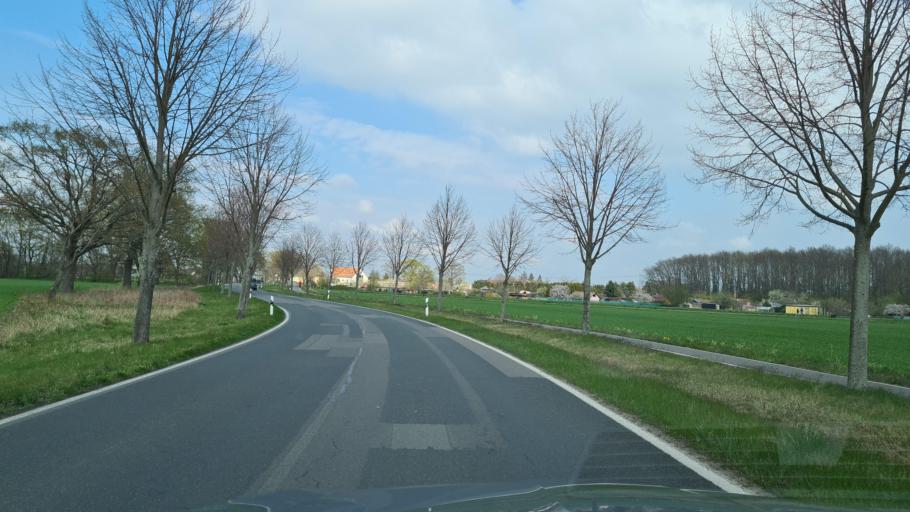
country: DE
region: Saxony
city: Wulknitz
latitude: 51.3855
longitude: 13.4352
